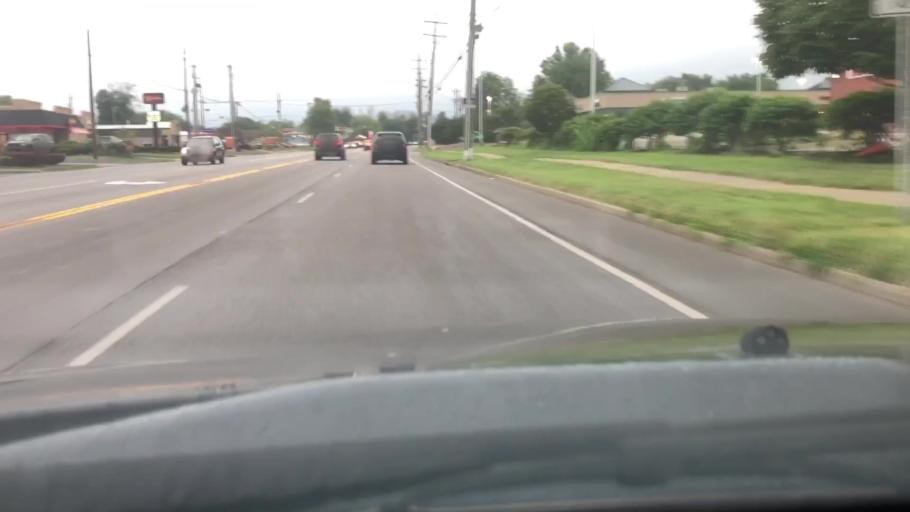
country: US
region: Kentucky
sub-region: Jefferson County
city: Hurstbourne Acres
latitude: 38.2055
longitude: -85.5800
